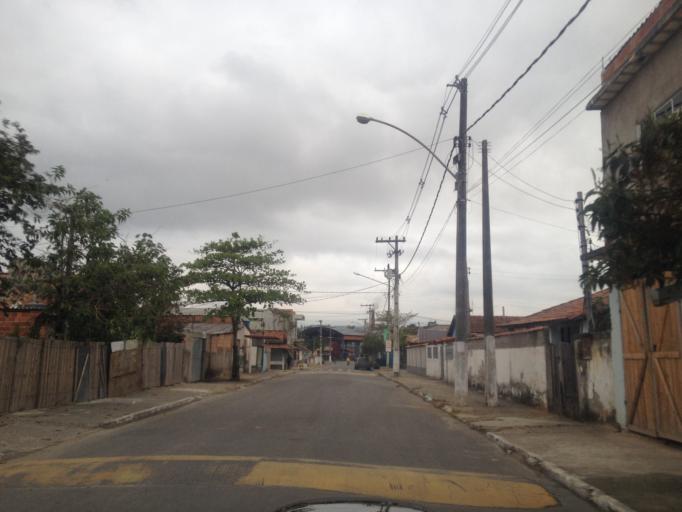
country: BR
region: Rio de Janeiro
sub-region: Porto Real
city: Porto Real
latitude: -22.4089
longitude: -44.2996
